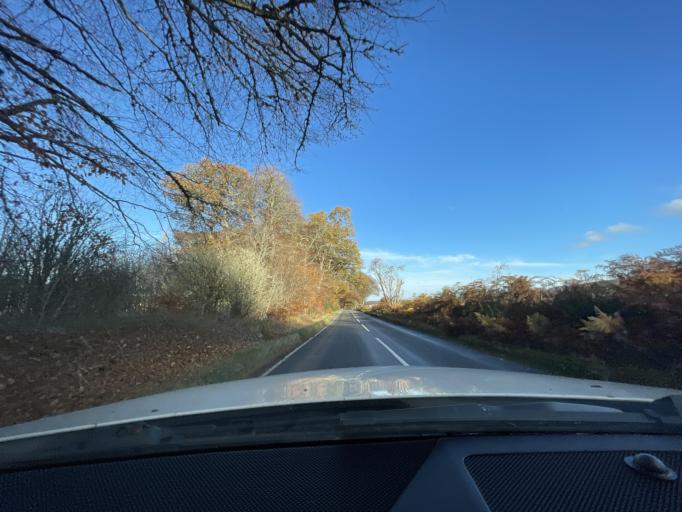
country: GB
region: Scotland
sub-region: Highland
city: Inverness
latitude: 57.4236
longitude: -4.2927
